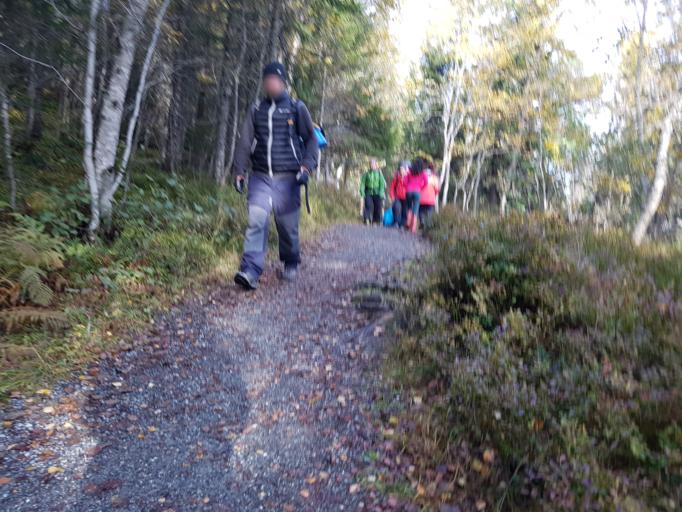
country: NO
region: Sor-Trondelag
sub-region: Trondheim
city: Trondheim
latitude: 63.4255
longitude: 10.2793
